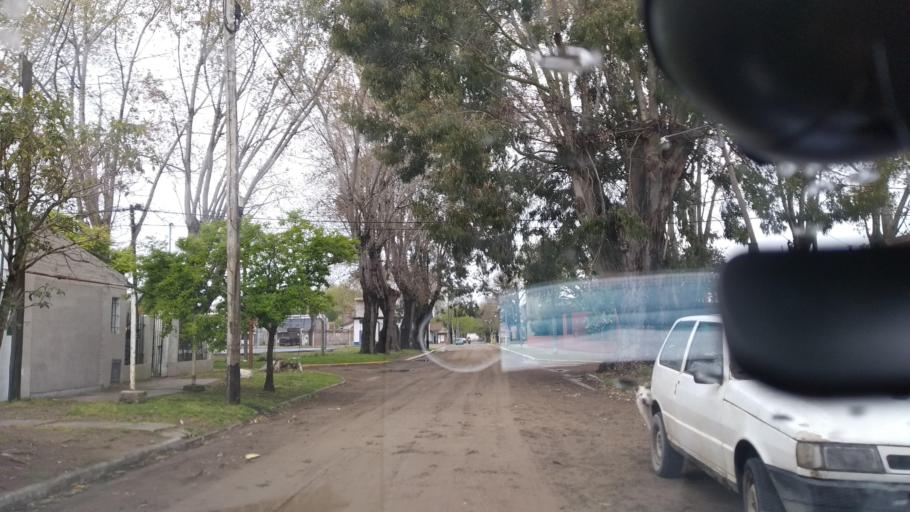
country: AR
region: Buenos Aires
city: Mar del Tuyu
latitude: -36.5300
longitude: -56.7129
